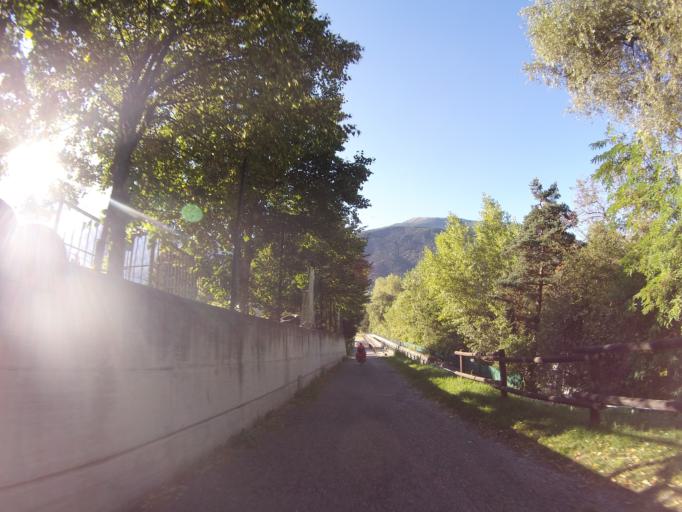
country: IT
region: Aosta Valley
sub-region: Valle d'Aosta
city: Montan-Angelin-Arensod
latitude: 45.7229
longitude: 7.2717
